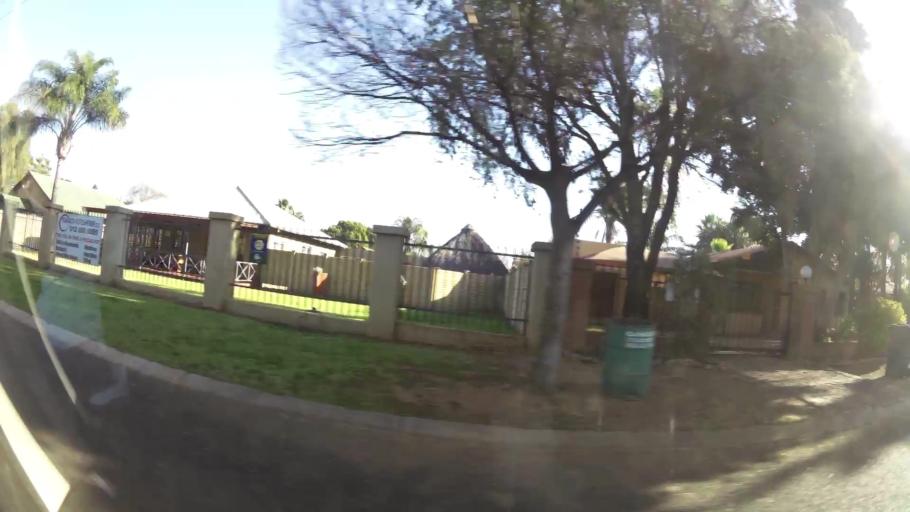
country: ZA
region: Gauteng
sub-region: City of Tshwane Metropolitan Municipality
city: Pretoria
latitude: -25.7097
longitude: 28.2566
